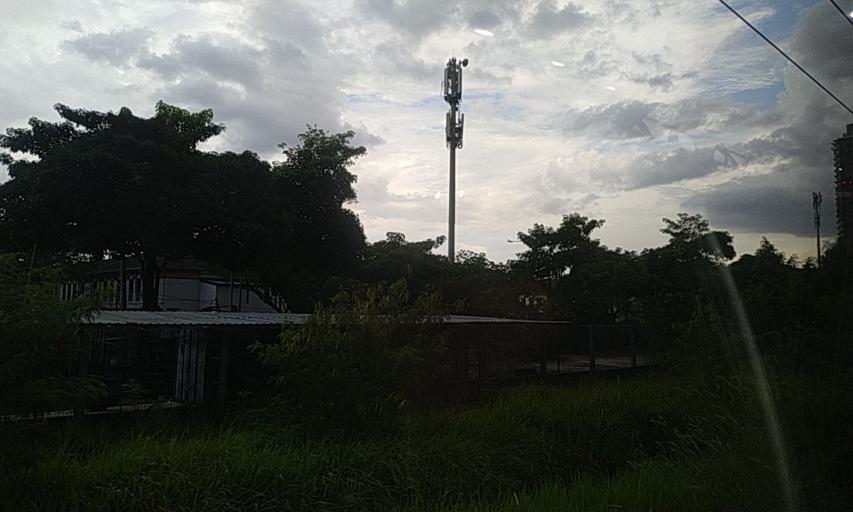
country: MY
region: Kuala Lumpur
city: Kuala Lumpur
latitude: 3.2167
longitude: 101.6723
